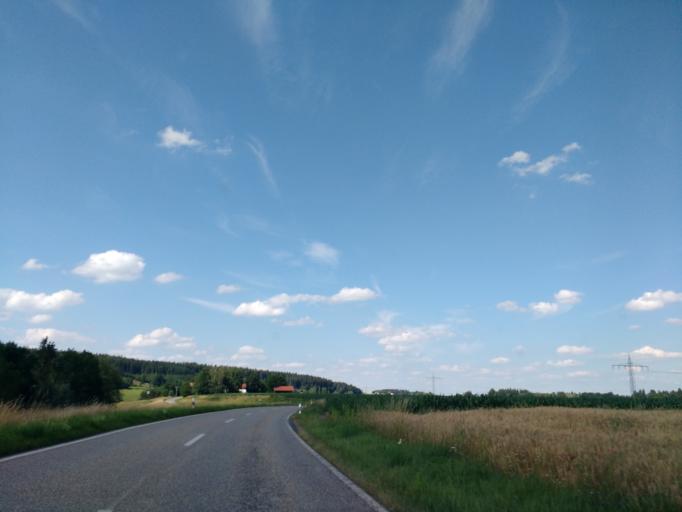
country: DE
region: Bavaria
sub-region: Upper Bavaria
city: Taufkirchen
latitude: 48.1222
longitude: 12.4222
